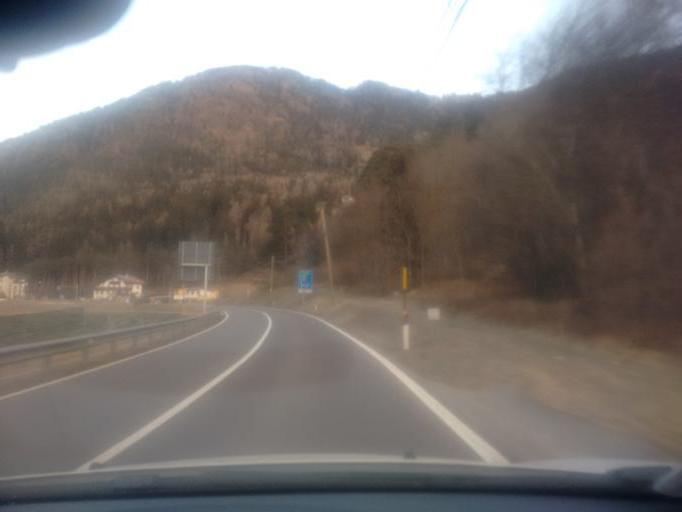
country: IT
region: Trentino-Alto Adige
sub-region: Bolzano
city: Campo di Trens
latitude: 46.8746
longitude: 11.4815
